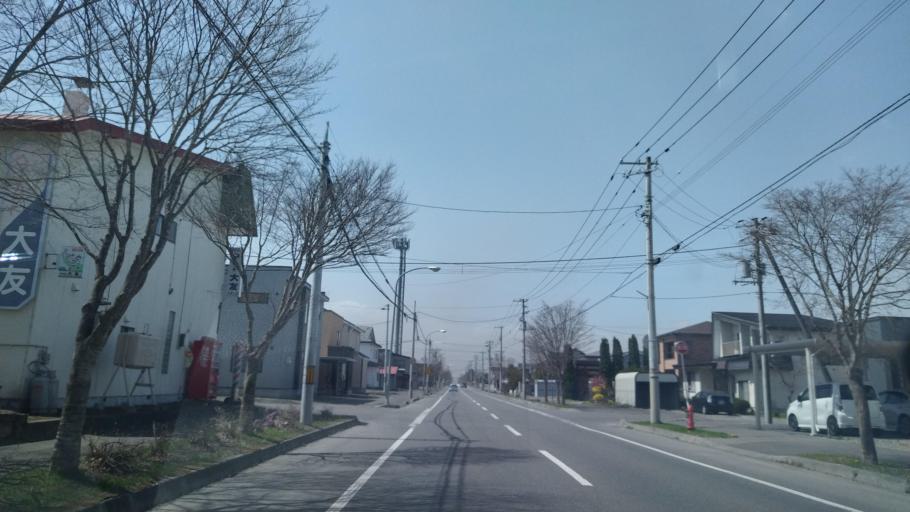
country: JP
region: Hokkaido
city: Obihiro
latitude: 42.9397
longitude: 143.1713
